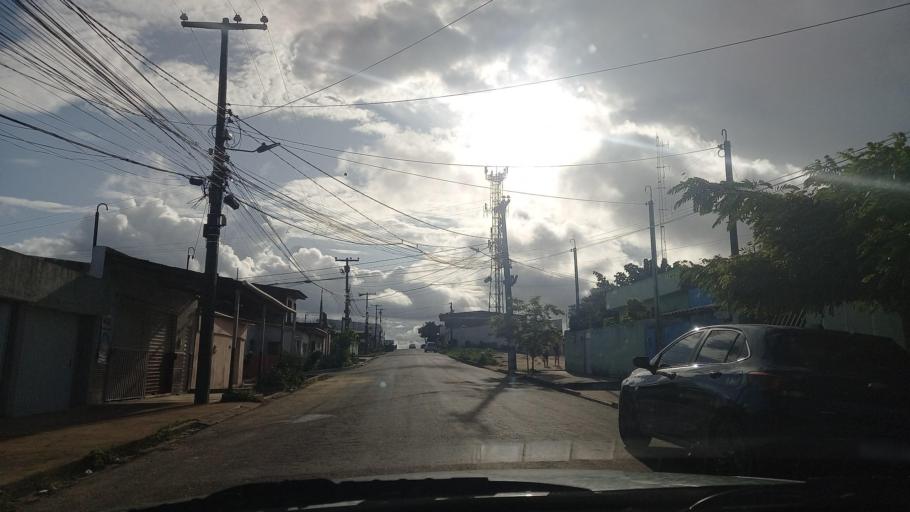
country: BR
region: Pernambuco
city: Garanhuns
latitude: -8.8991
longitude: -36.4962
